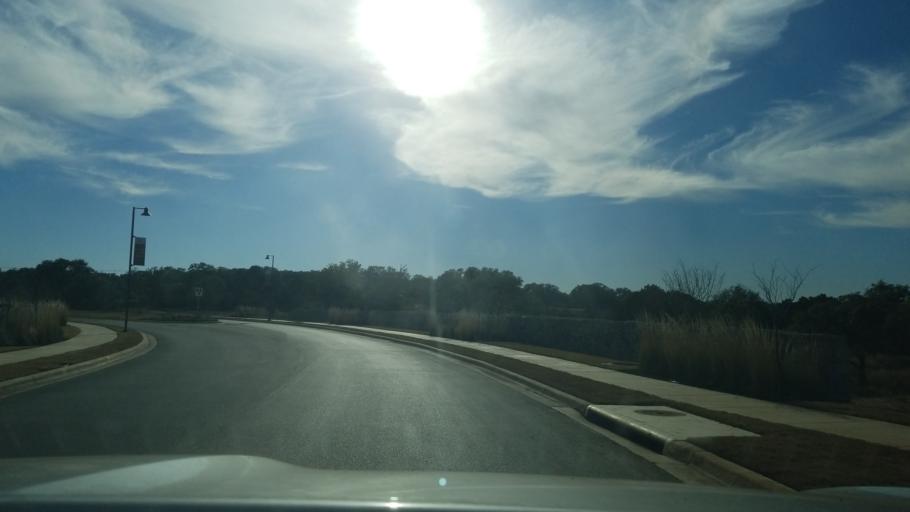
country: US
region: Texas
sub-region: Comal County
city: Canyon Lake
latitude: 29.7760
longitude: -98.2890
